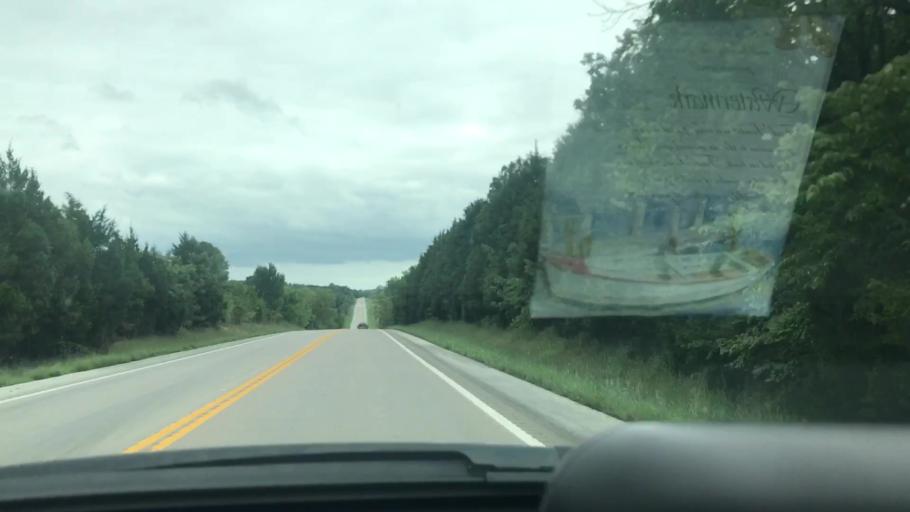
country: US
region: Missouri
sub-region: Dallas County
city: Buffalo
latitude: 37.7147
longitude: -93.1178
